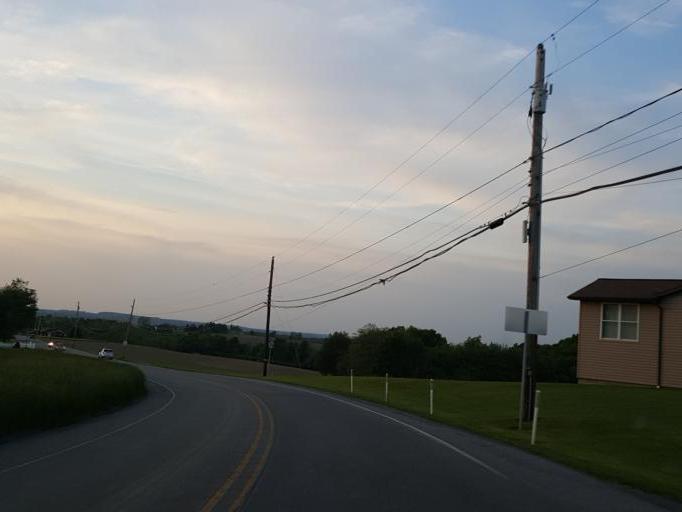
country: US
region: Pennsylvania
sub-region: Cambria County
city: Patton
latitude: 40.5914
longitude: -78.6025
